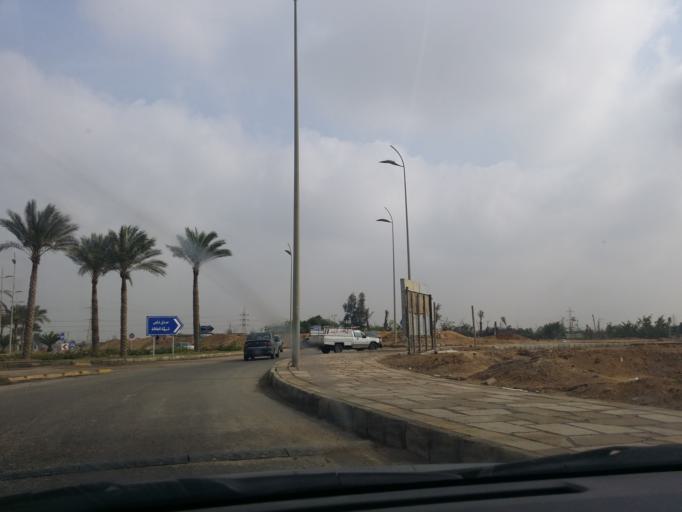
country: EG
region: Muhafazat al Qalyubiyah
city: Al Khankah
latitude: 30.1101
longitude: 31.6313
